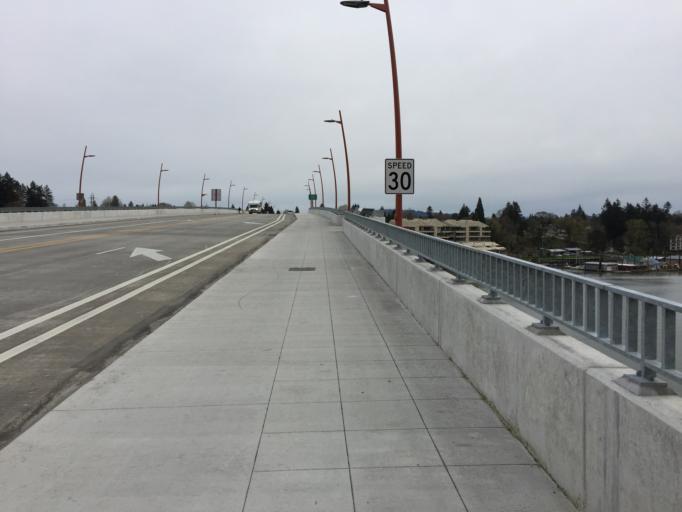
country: US
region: Oregon
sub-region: Clackamas County
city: Milwaukie
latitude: 45.4642
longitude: -122.6672
